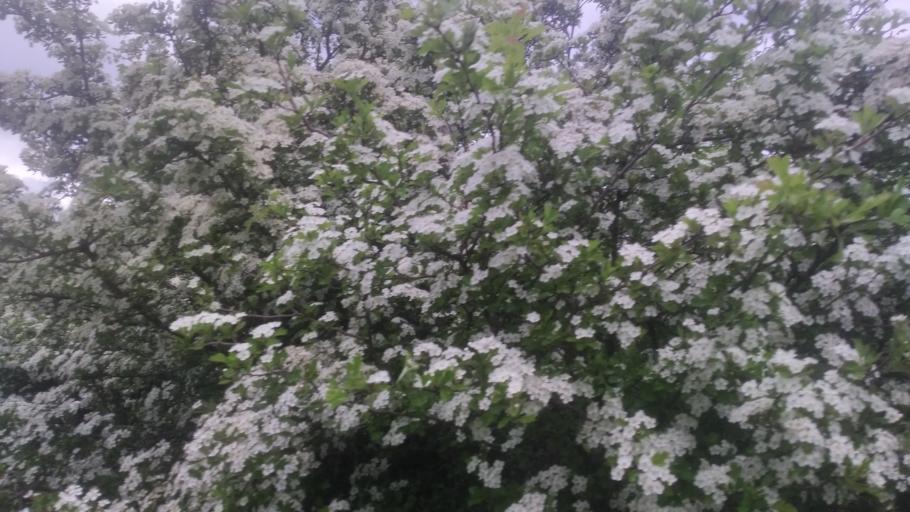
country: HU
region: Pest
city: Pilisborosjeno
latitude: 47.5547
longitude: 18.9755
